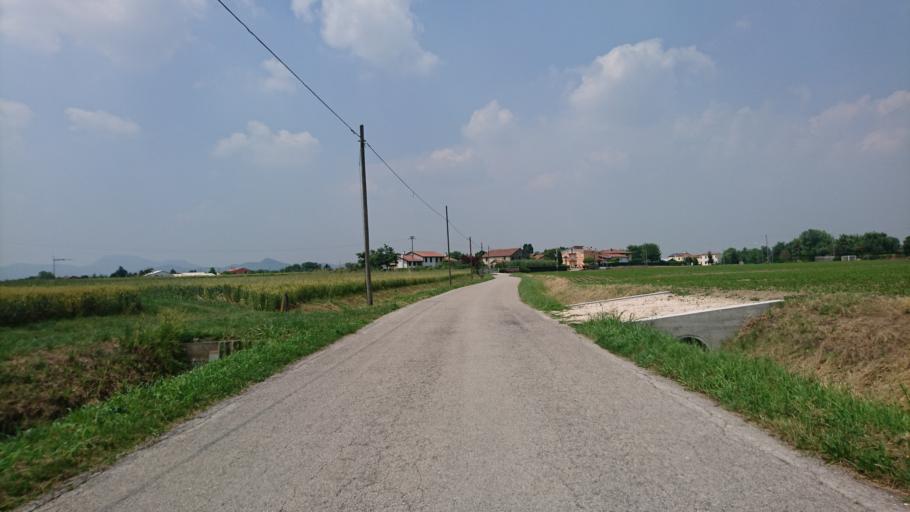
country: IT
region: Veneto
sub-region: Provincia di Padova
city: Cartura
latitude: 45.2767
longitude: 11.8544
